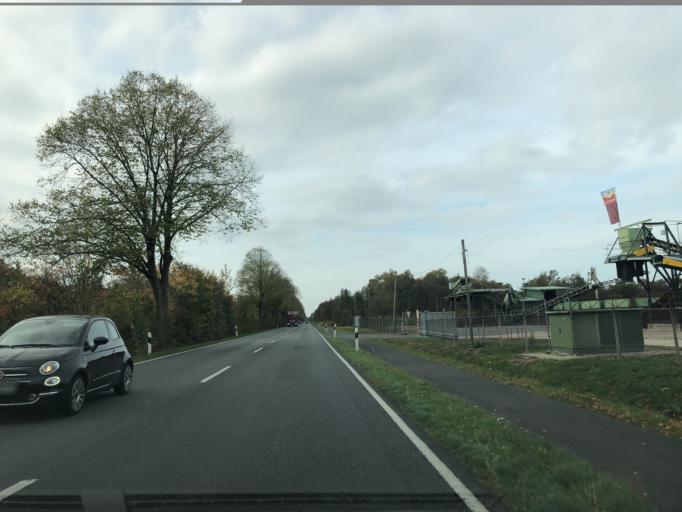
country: DE
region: Lower Saxony
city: Esterwegen
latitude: 53.0167
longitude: 7.6316
